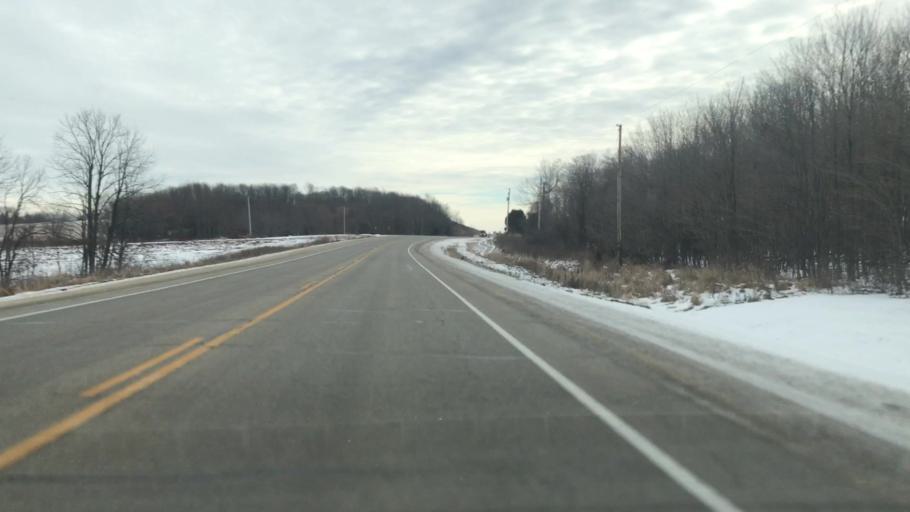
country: US
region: Wisconsin
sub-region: Dodge County
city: Mayville
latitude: 43.4400
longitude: -88.4825
